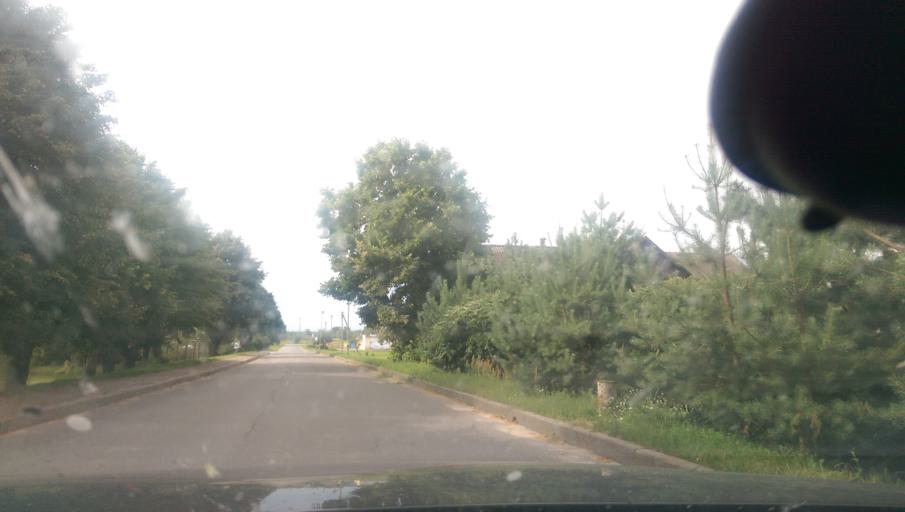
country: LT
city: Rusne
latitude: 55.2947
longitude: 21.3735
